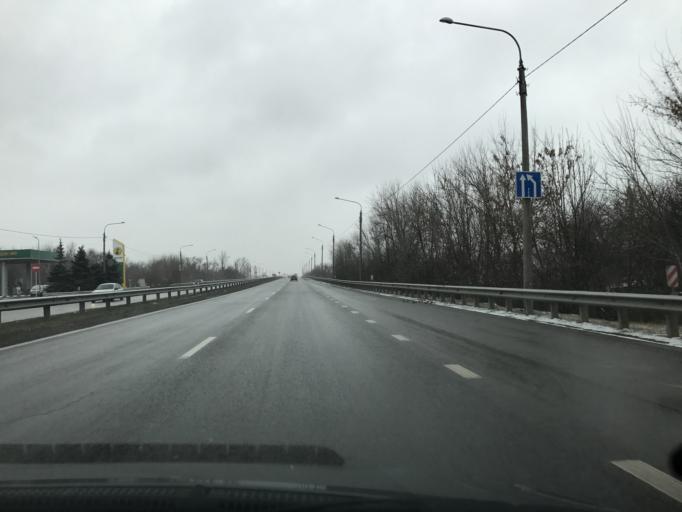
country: RU
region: Rostov
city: Bataysk
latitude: 47.1250
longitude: 39.7733
